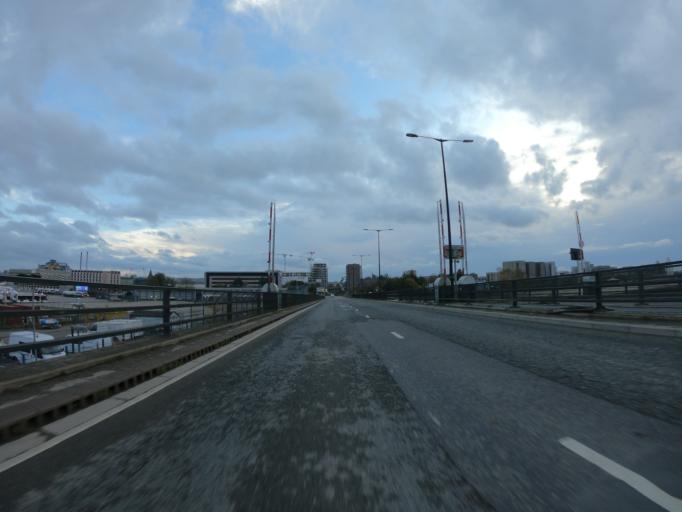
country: GB
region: England
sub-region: Greater London
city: East Ham
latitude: 51.5061
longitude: 0.0399
